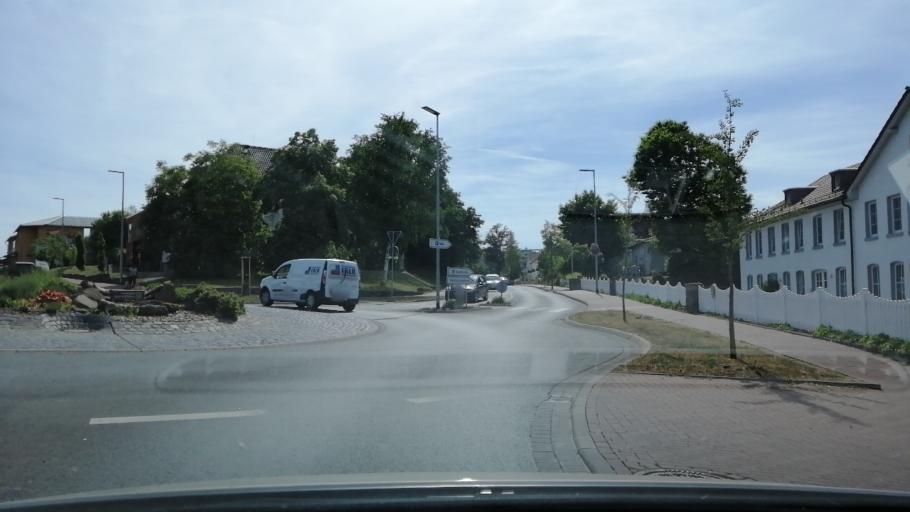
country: DE
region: Hesse
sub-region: Regierungsbezirk Kassel
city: Bad Wildungen
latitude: 51.1208
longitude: 9.1211
